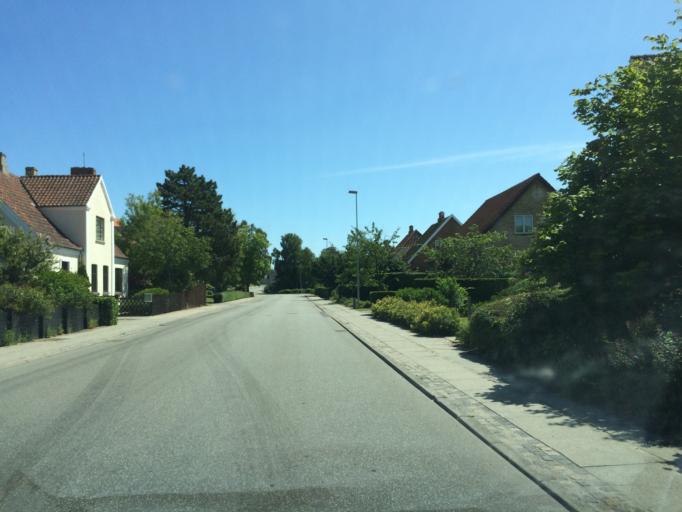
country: DK
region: Central Jutland
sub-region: Samso Kommune
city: Tranebjerg
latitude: 55.8321
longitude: 10.5884
